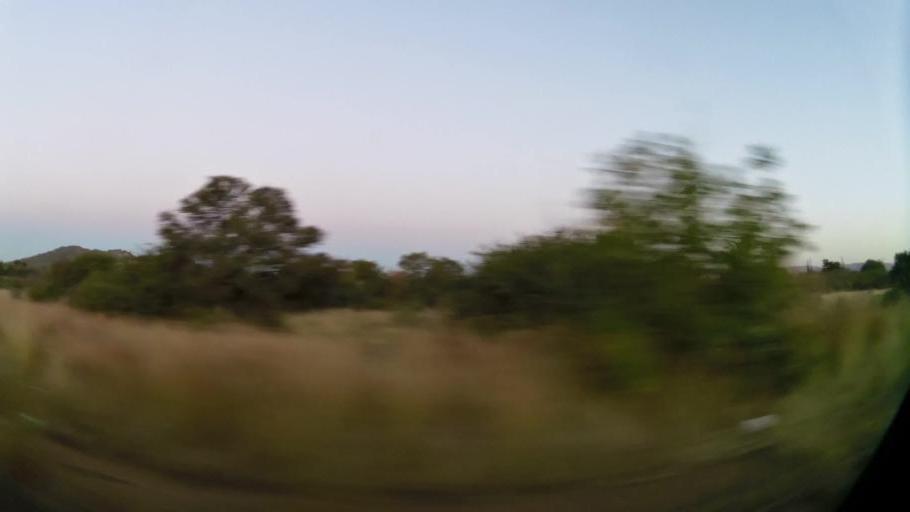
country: ZA
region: North-West
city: Ga-Rankuwa
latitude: -25.6331
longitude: 27.9561
